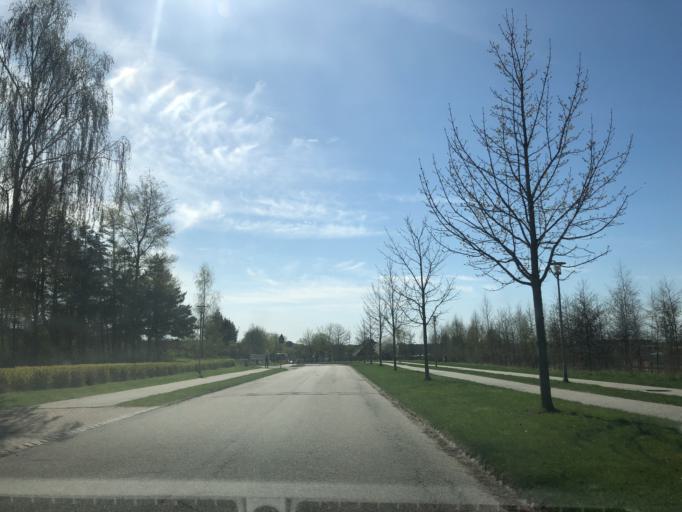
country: DK
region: Zealand
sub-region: Ringsted Kommune
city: Ringsted
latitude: 55.4273
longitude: 11.7827
